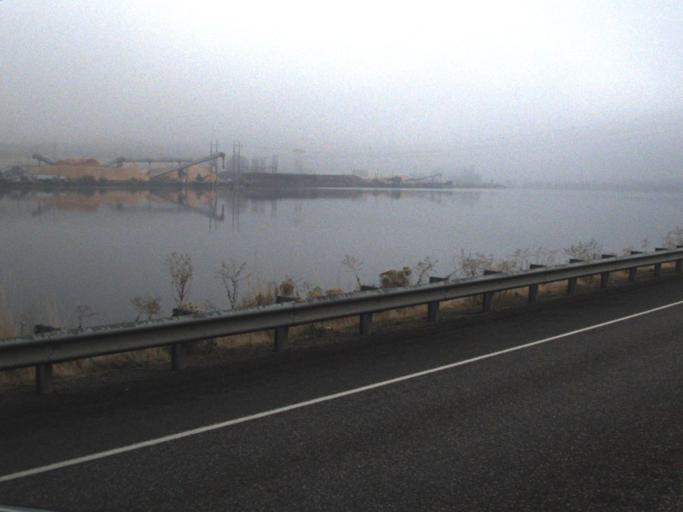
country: US
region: Washington
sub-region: Asotin County
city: Clarkston Heights-Vineland
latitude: 46.4203
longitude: -117.1174
